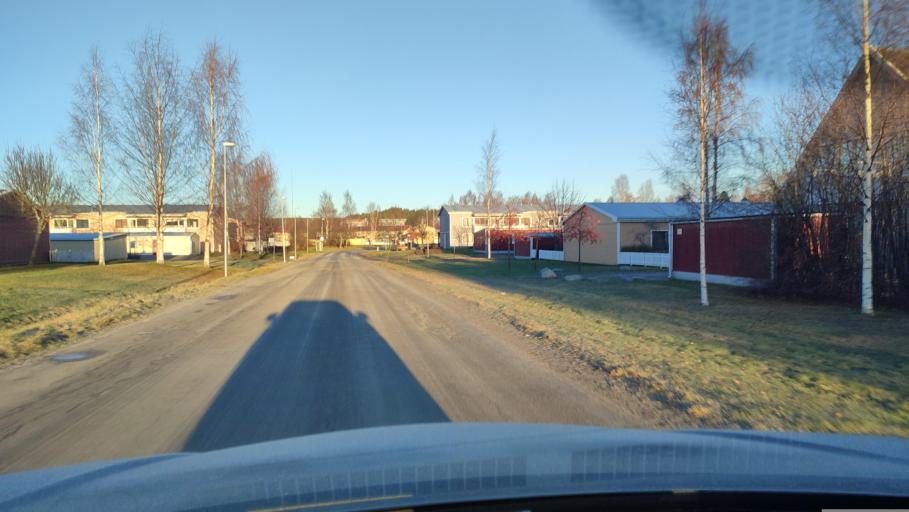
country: SE
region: Vaesterbotten
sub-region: Skelleftea Kommun
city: Skelleftea
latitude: 64.7430
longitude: 20.9836
